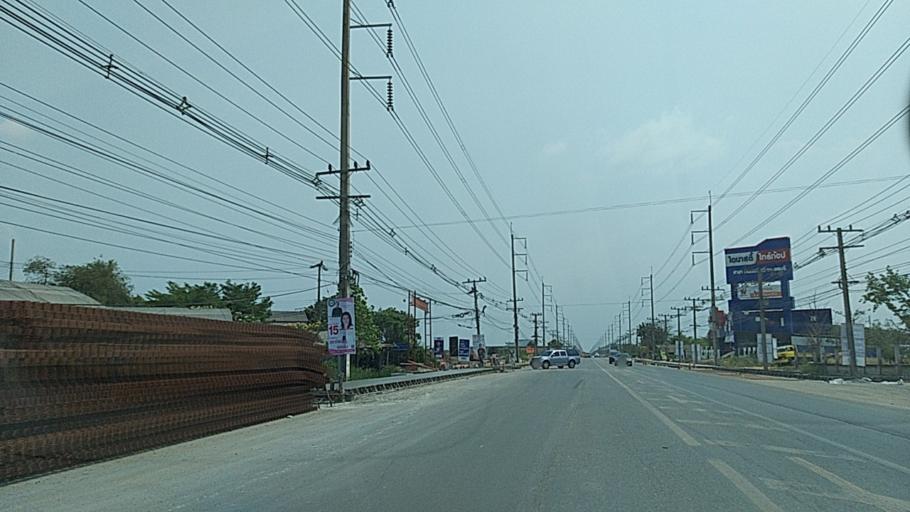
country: TH
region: Chon Buri
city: Phanat Nikhom
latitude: 13.4820
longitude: 101.1679
